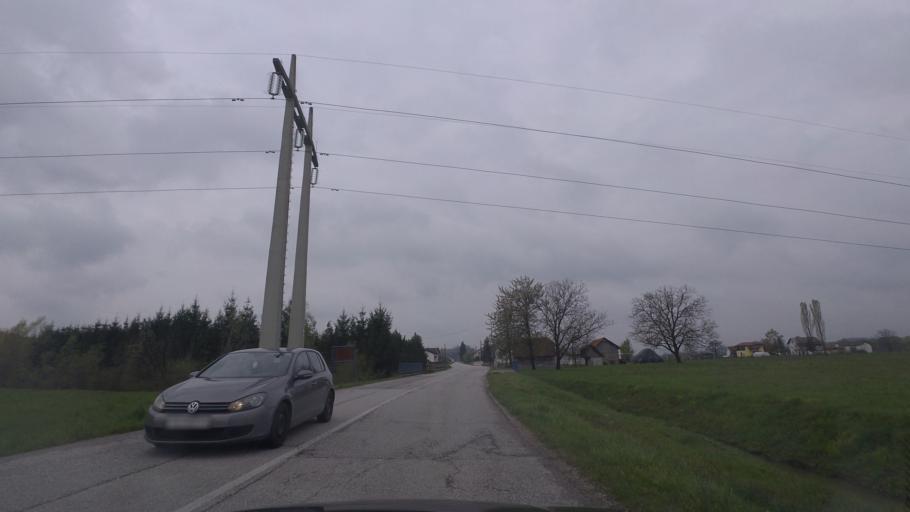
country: HR
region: Zagrebacka
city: Jastrebarsko
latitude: 45.6126
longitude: 15.5930
